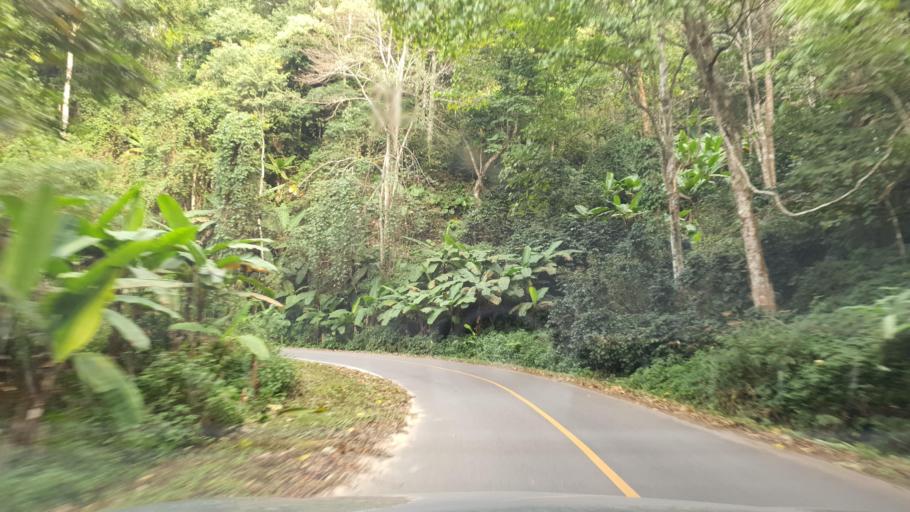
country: TH
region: Lampang
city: Mueang Pan
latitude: 18.9348
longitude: 99.3822
